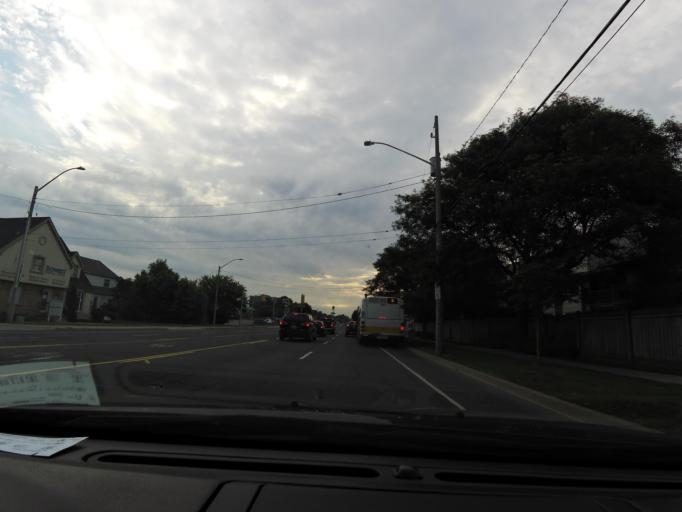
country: CA
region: Ontario
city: Hamilton
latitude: 43.2202
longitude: -79.7737
